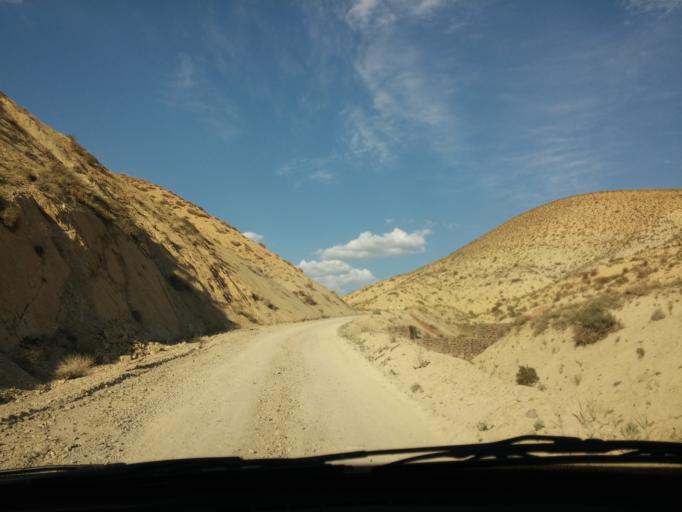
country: IR
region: Tehran
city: Damavand
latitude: 35.5346
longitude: 52.2024
